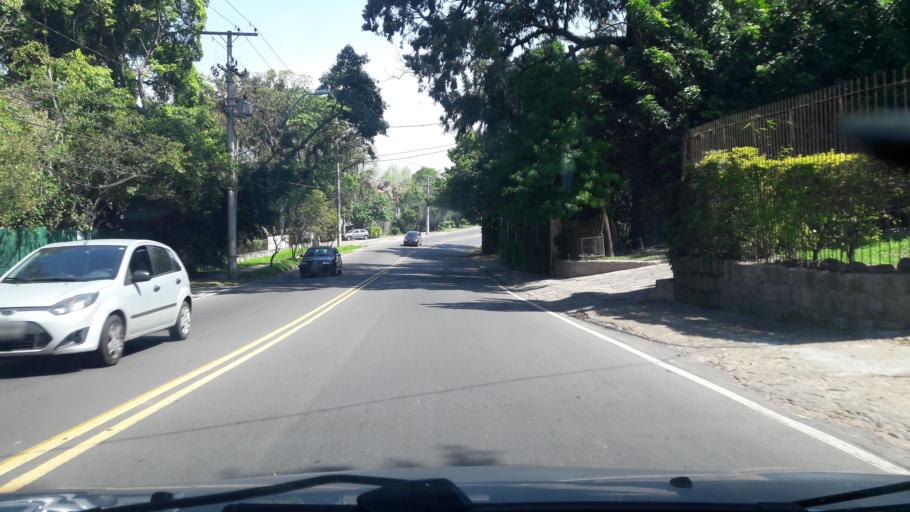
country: BR
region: Rio Grande do Sul
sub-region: Guaiba
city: Guaiba
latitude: -30.1229
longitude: -51.2507
